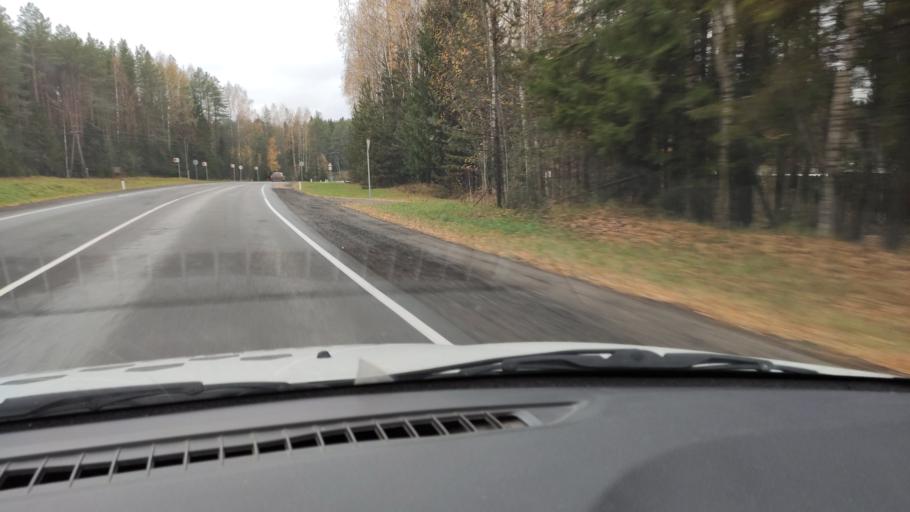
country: RU
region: Kirov
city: Belaya Kholunitsa
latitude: 58.9040
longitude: 50.9497
